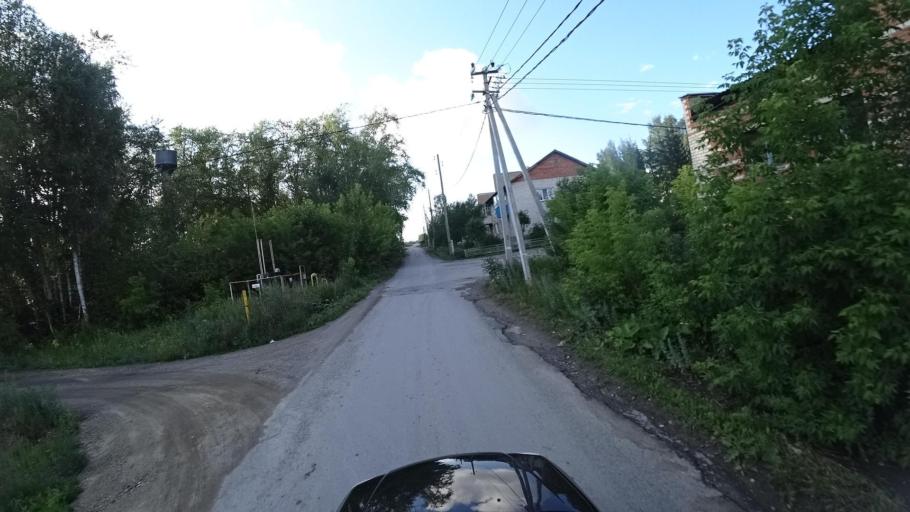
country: RU
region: Sverdlovsk
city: Obukhovskoye
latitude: 56.8474
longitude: 62.6543
